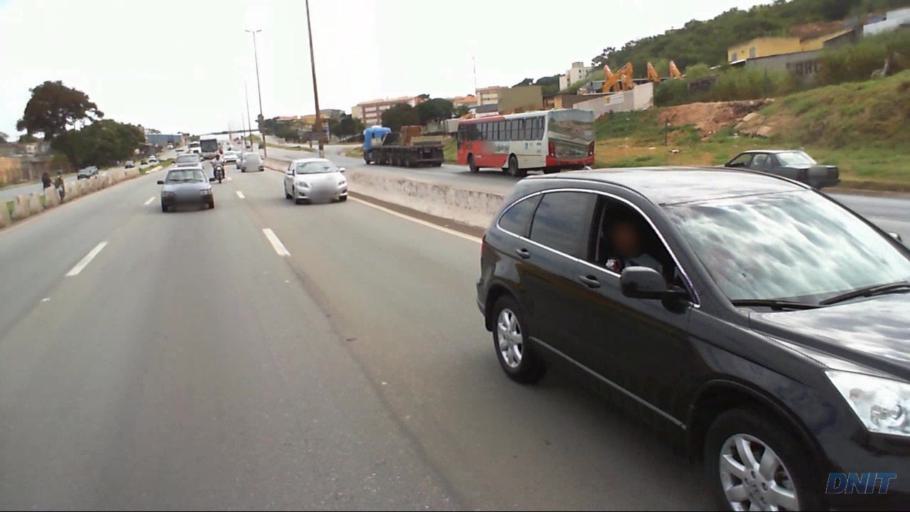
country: BR
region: Minas Gerais
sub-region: Belo Horizonte
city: Belo Horizonte
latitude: -19.8579
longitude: -43.9054
